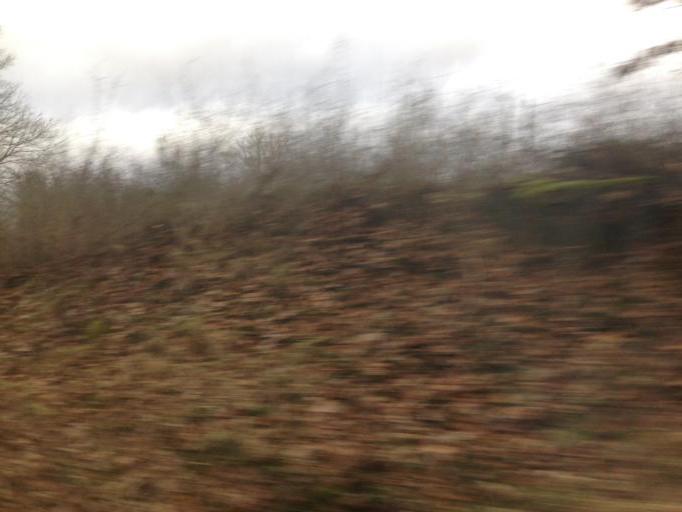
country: DE
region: Hesse
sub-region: Regierungsbezirk Giessen
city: Lich
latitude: 50.5194
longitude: 8.7925
